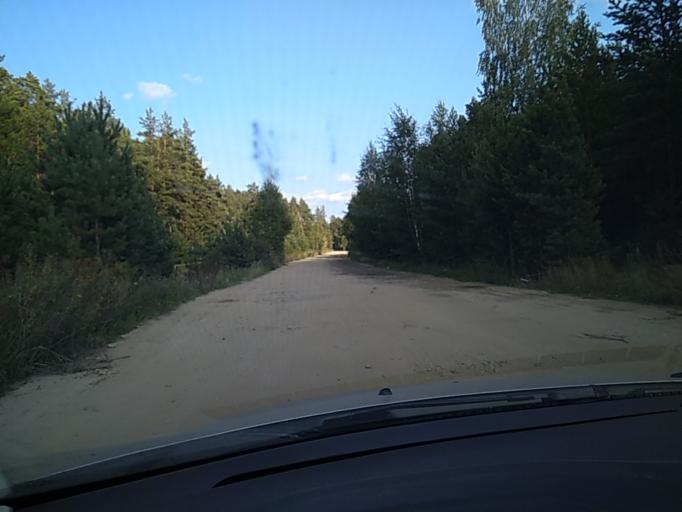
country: RU
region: Chelyabinsk
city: Kyshtym
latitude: 55.6862
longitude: 60.5631
